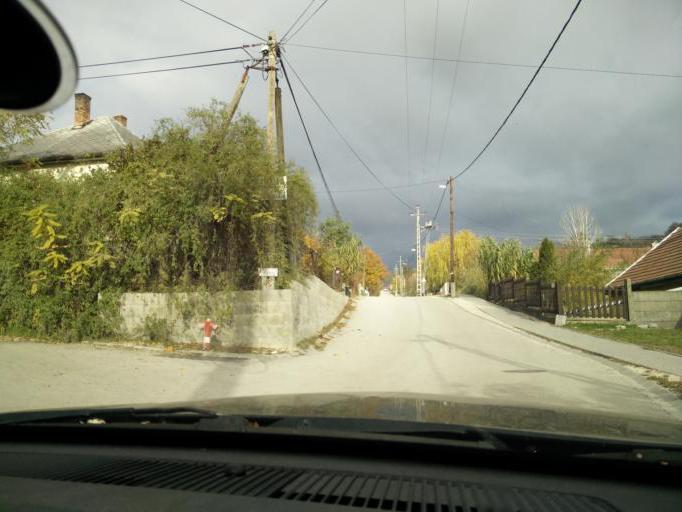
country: HU
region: Komarom-Esztergom
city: Piliscsev
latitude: 47.6568
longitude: 18.7965
